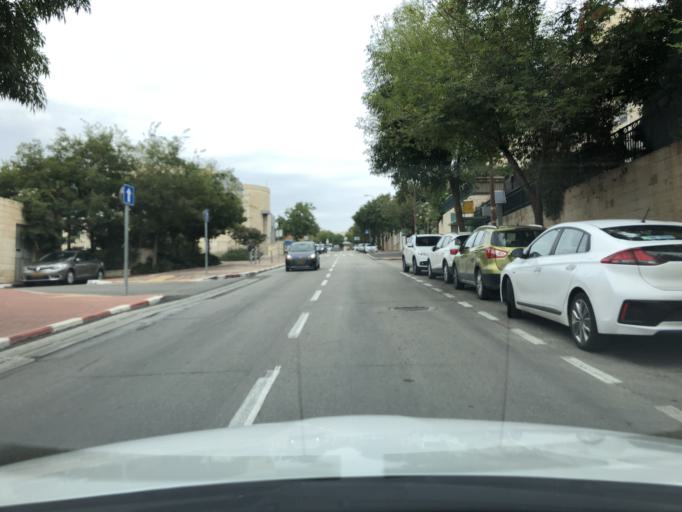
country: IL
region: Central District
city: Modiin
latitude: 31.9046
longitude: 35.0080
